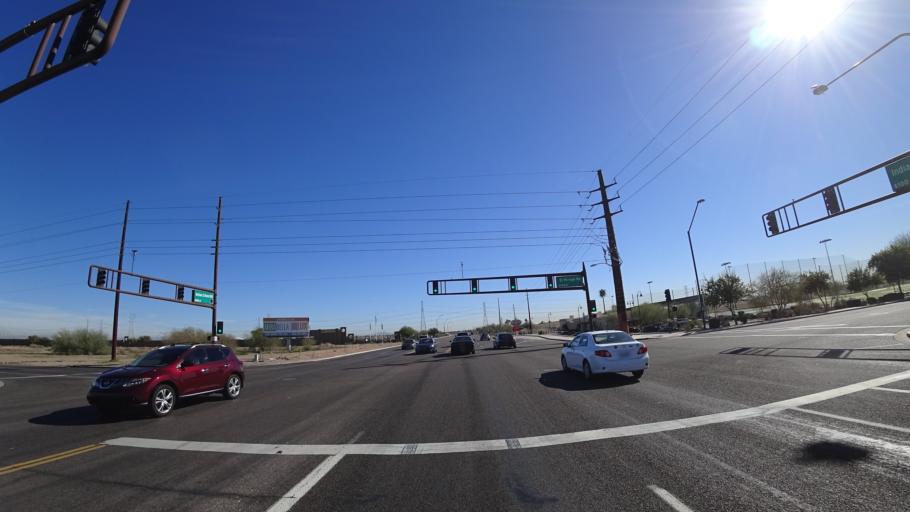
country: US
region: Arizona
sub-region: Maricopa County
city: Litchfield Park
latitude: 33.4932
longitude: -112.3240
